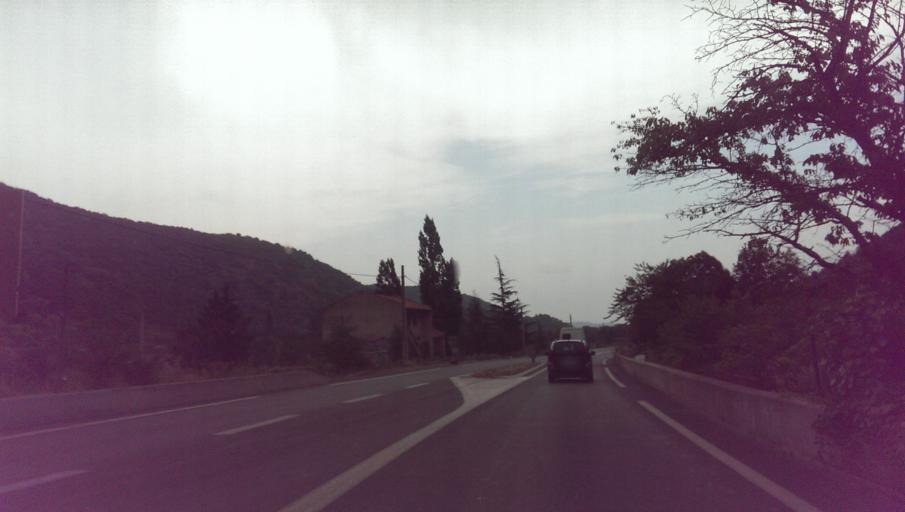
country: FR
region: Languedoc-Roussillon
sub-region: Departement des Pyrenees-Orientales
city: Ria-Sirach
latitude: 42.6010
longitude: 2.3826
